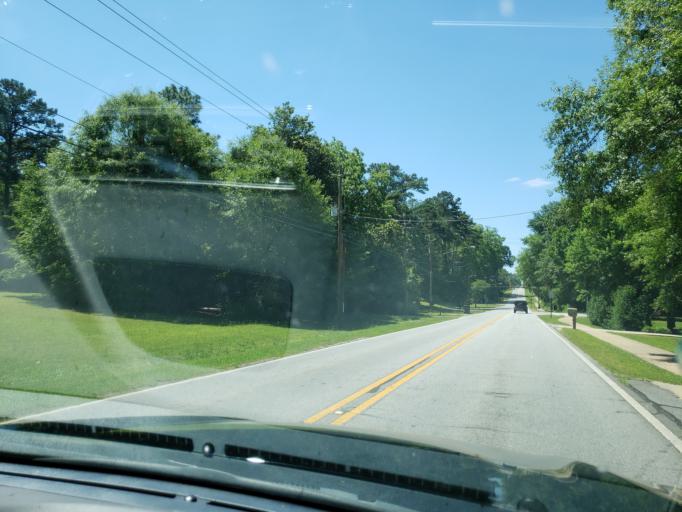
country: US
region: Alabama
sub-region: Lee County
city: Auburn
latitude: 32.6245
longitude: -85.4819
